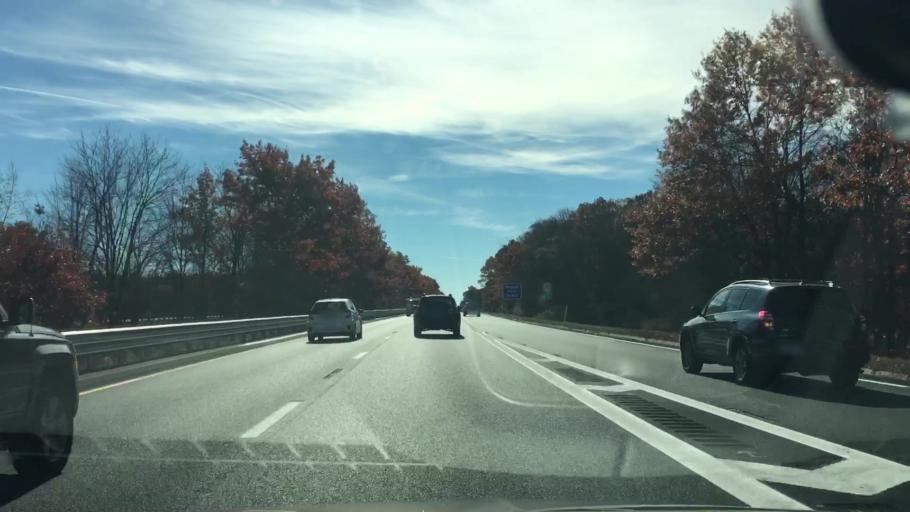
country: US
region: Massachusetts
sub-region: Franklin County
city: South Deerfield
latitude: 42.4630
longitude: -72.6167
